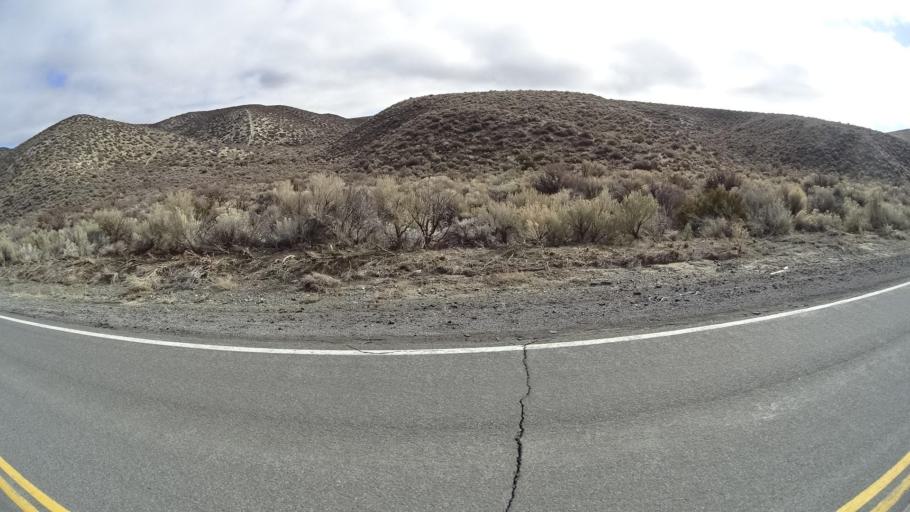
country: US
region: Nevada
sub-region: Washoe County
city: Cold Springs
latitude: 39.8061
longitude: -119.9317
